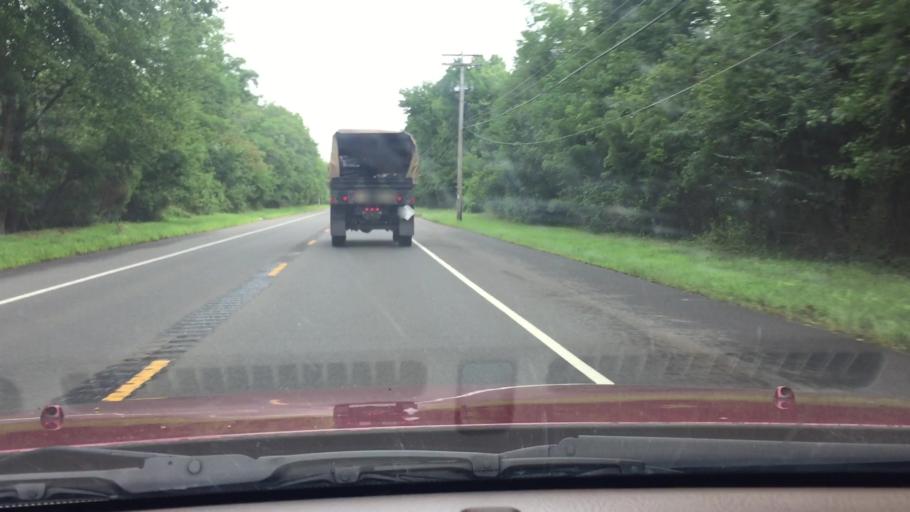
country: US
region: New Jersey
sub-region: Burlington County
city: Fort Dix
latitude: 40.0402
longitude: -74.6445
